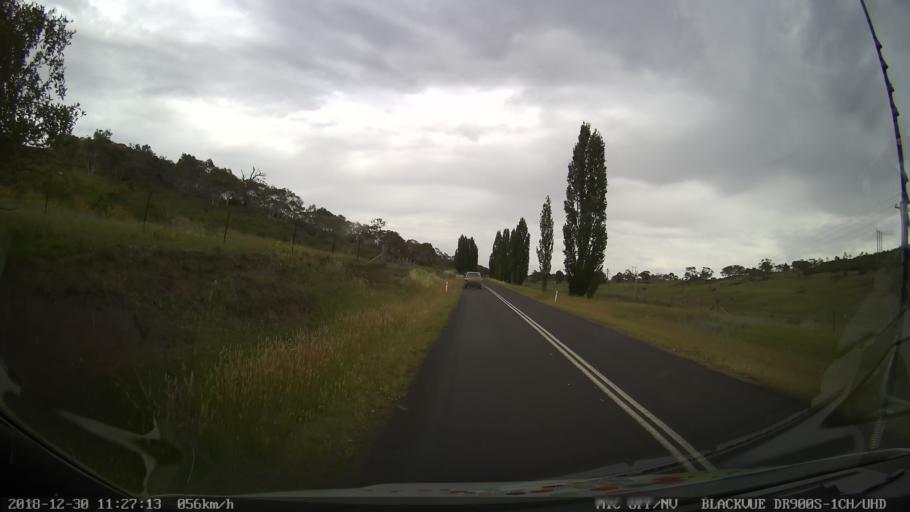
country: AU
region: New South Wales
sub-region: Snowy River
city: Jindabyne
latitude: -36.4624
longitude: 148.6284
